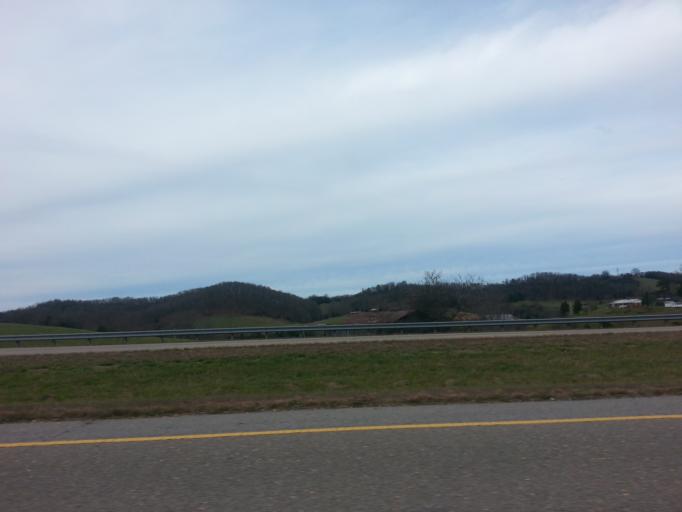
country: US
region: Tennessee
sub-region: Cocke County
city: Newport
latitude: 36.0148
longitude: -83.0506
